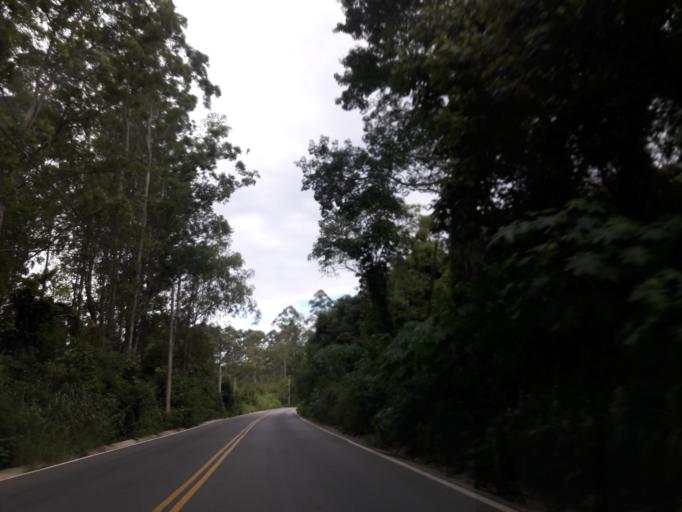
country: BR
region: Sao Paulo
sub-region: Aruja
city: Aruja
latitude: -23.3728
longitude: -46.4262
